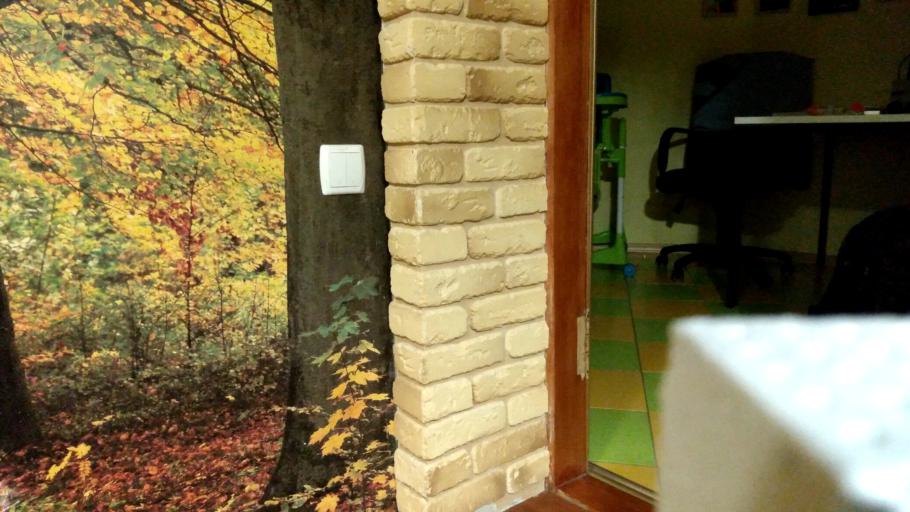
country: RU
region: Arkhangelskaya
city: Kargopol'
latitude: 61.5881
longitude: 37.7483
